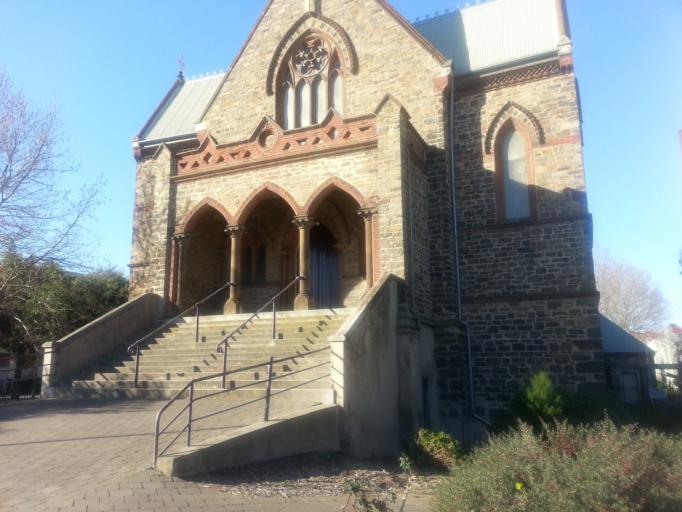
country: AU
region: South Australia
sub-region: Port Adelaide Enfield
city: Birkenhead
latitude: -34.8470
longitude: 138.5074
